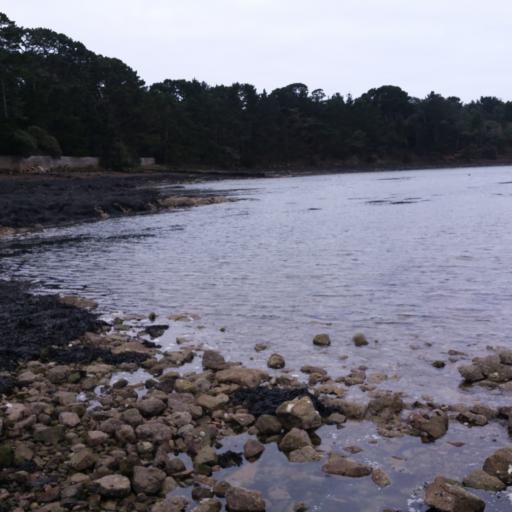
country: FR
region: Brittany
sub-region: Departement du Morbihan
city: Larmor-Baden
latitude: 47.5824
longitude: -2.8896
